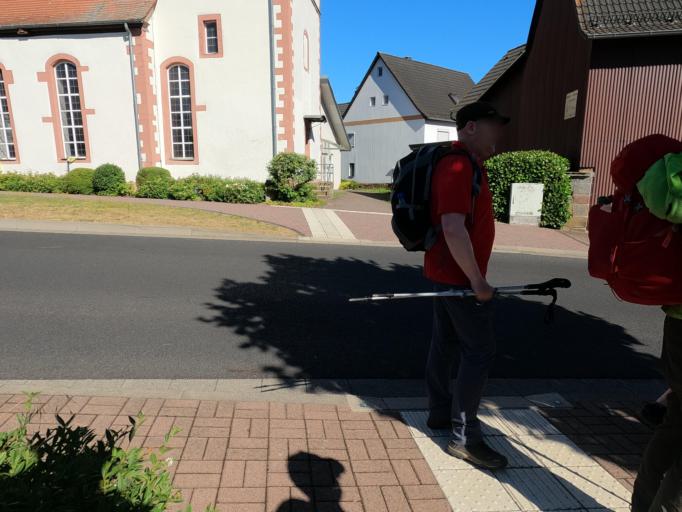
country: DE
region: Bavaria
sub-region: Regierungsbezirk Unterfranken
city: Zeitlofs
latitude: 50.3118
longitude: 9.6699
